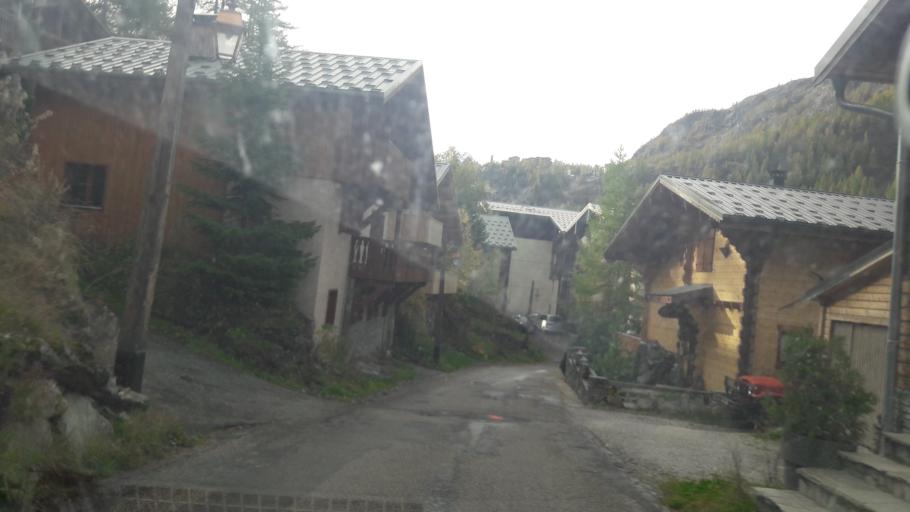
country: FR
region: Rhone-Alpes
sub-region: Departement de la Savoie
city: Tignes
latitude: 45.5090
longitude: 6.9210
